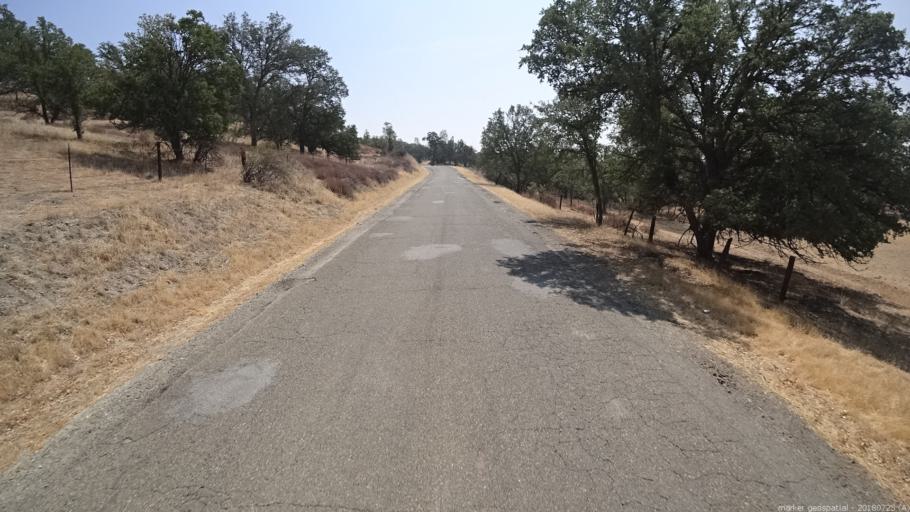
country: US
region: California
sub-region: San Luis Obispo County
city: Shandon
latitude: 35.8727
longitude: -120.4105
